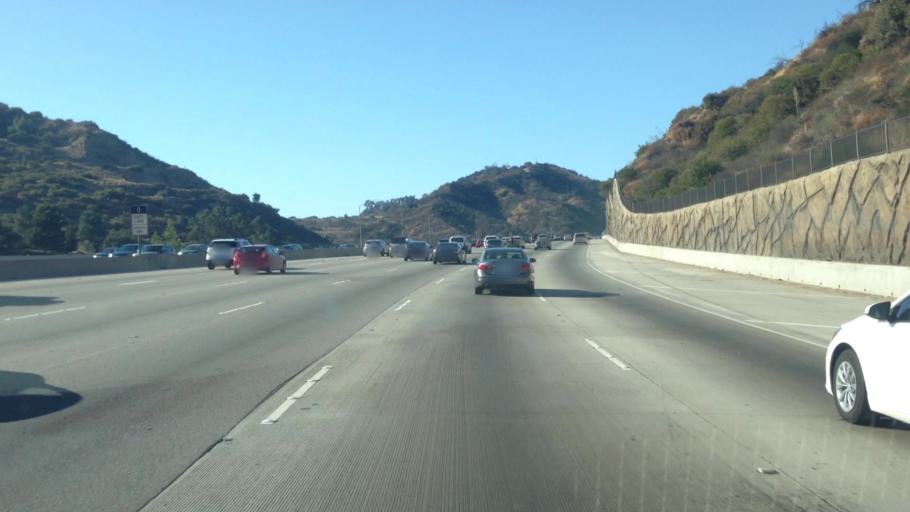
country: US
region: California
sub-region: Los Angeles County
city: Sherman Oaks
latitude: 34.1121
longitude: -118.4813
